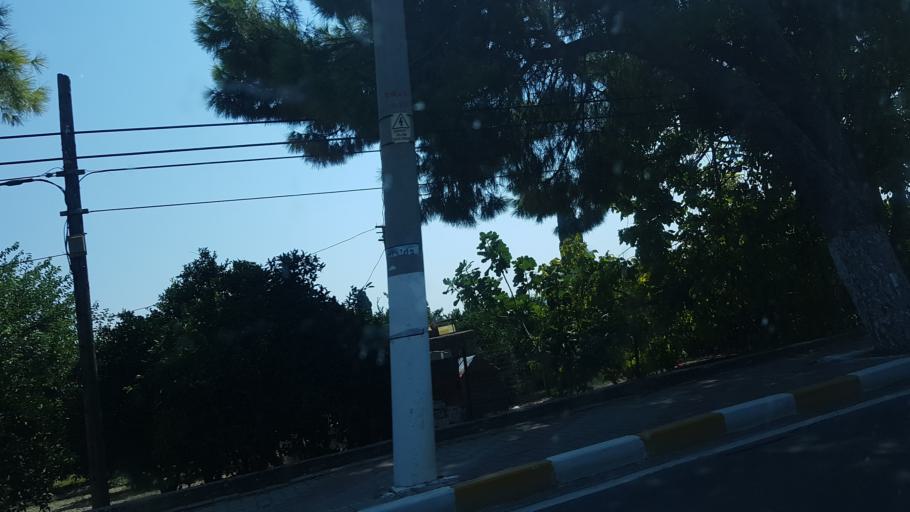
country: TR
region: Izmir
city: Urla
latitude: 38.3452
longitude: 26.7717
